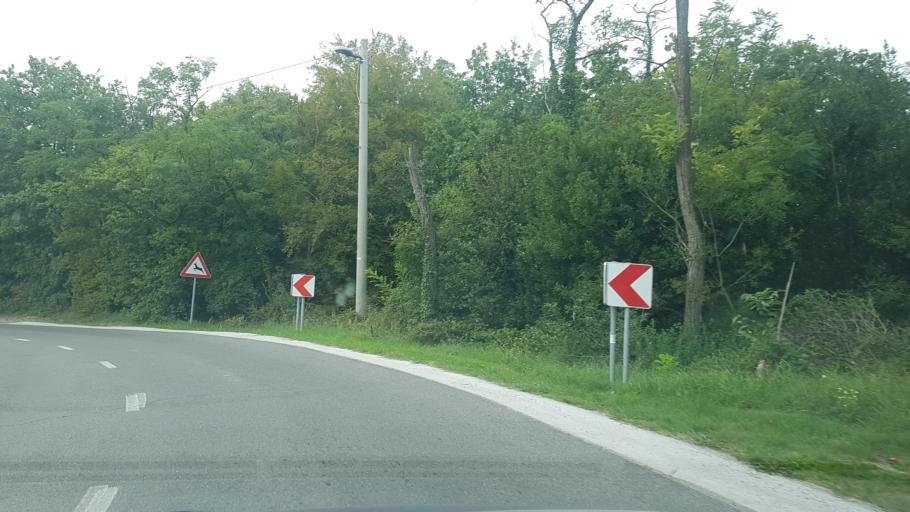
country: SI
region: Koper-Capodistria
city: Spodnje Skofije
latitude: 45.5729
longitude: 13.7990
